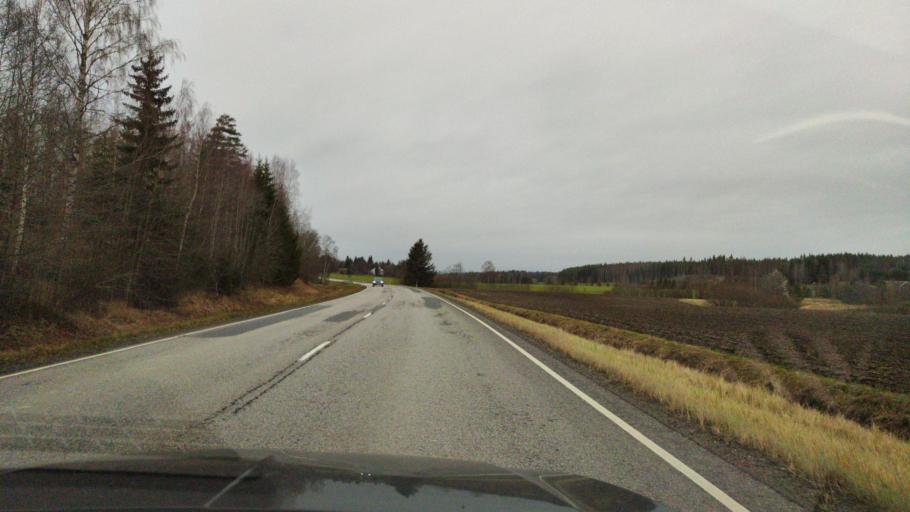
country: FI
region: Varsinais-Suomi
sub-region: Loimaa
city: Ylaene
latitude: 60.8496
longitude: 22.4364
